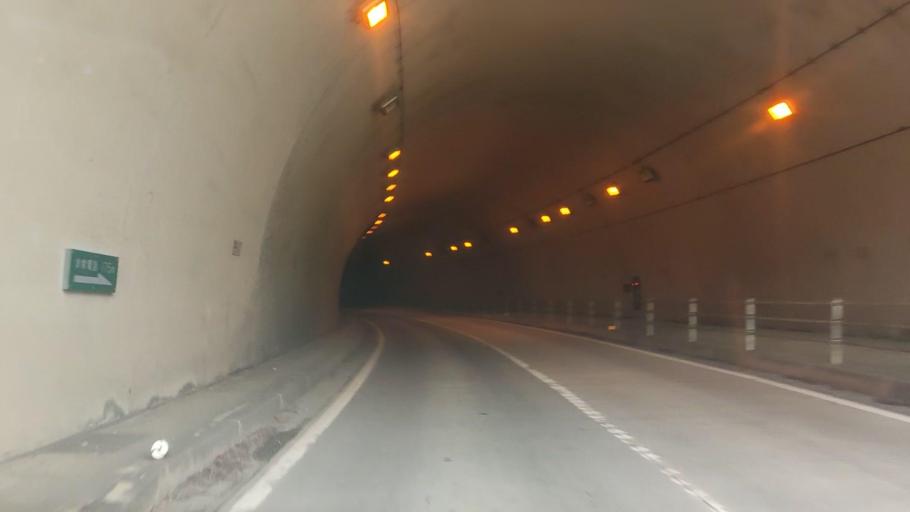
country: JP
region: Kumamoto
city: Hitoyoshi
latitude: 32.3933
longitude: 130.8275
